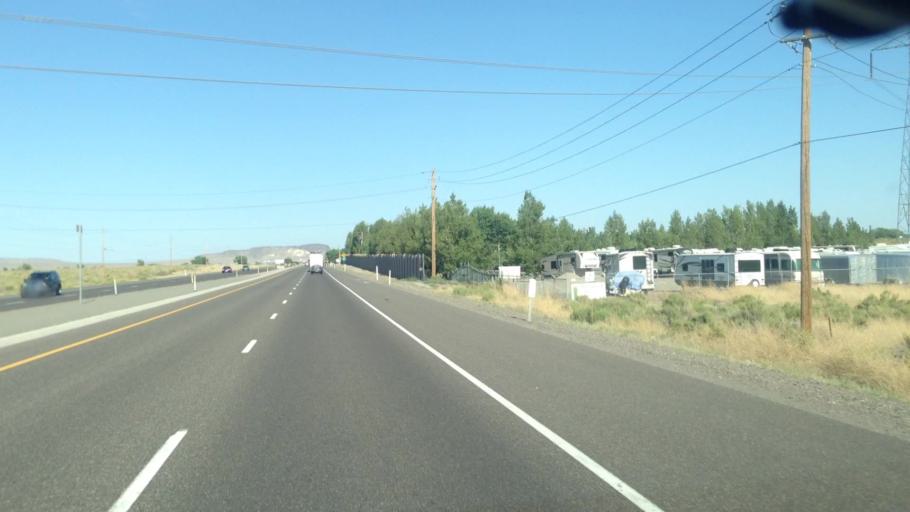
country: US
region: Nevada
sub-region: Lyon County
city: Fernley
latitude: 39.5936
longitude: -119.1624
